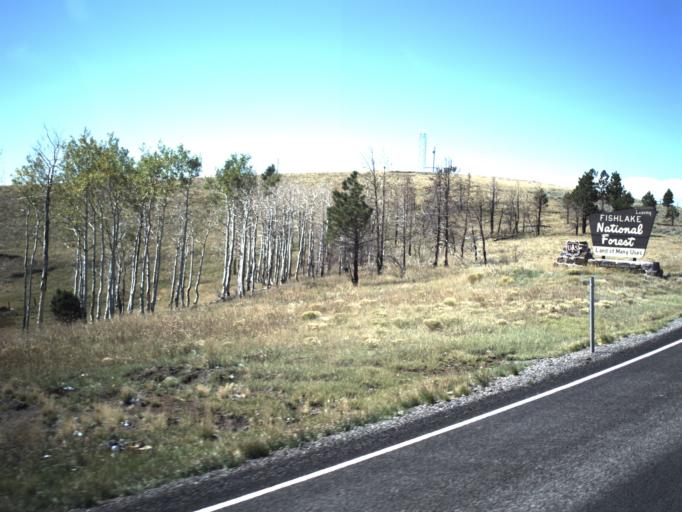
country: US
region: Utah
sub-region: Wayne County
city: Loa
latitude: 38.5141
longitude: -111.7819
